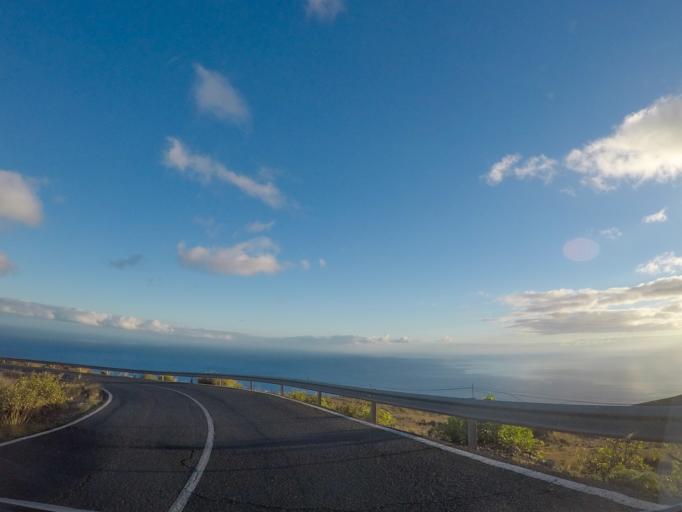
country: ES
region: Canary Islands
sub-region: Provincia de Santa Cruz de Tenerife
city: Alajero
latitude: 28.0511
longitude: -17.2333
